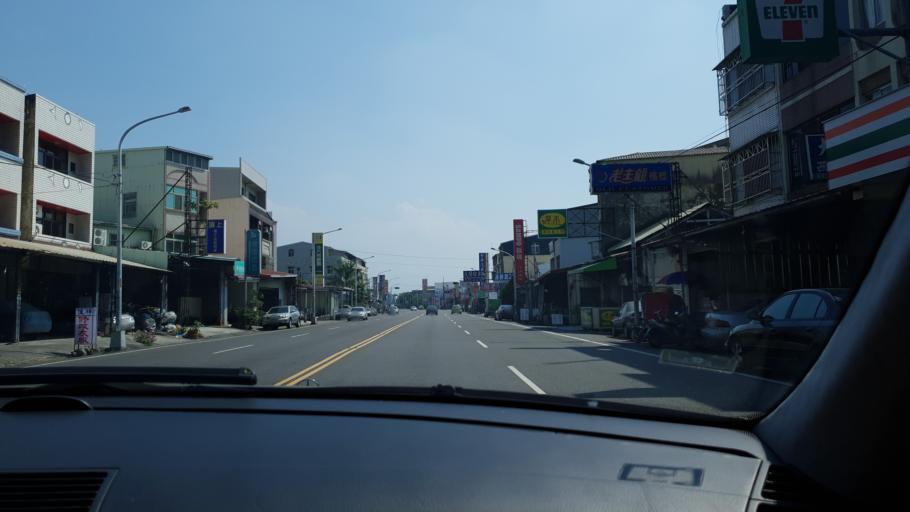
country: TW
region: Taiwan
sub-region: Yunlin
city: Douliu
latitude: 23.7217
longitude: 120.5260
